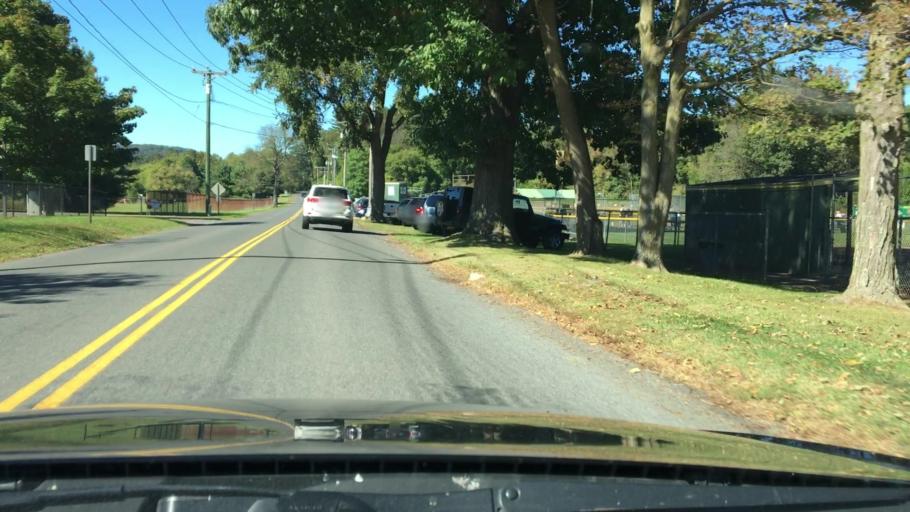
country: US
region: Connecticut
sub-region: Litchfield County
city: New Milford
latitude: 41.5877
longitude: -73.4401
